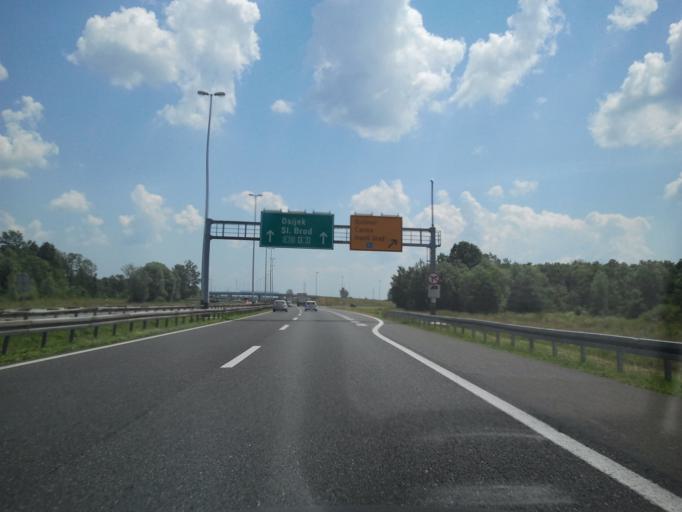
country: HR
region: Zagrebacka
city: Lupoglav
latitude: 45.6876
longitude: 16.3829
